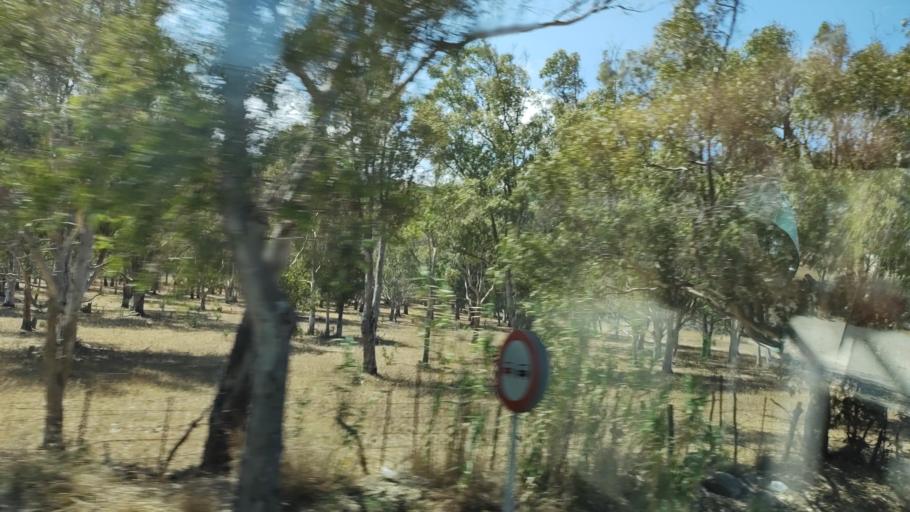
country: ES
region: Andalusia
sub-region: Provincia de Cadiz
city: La Linea de la Concepcion
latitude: 36.1966
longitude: -5.3472
